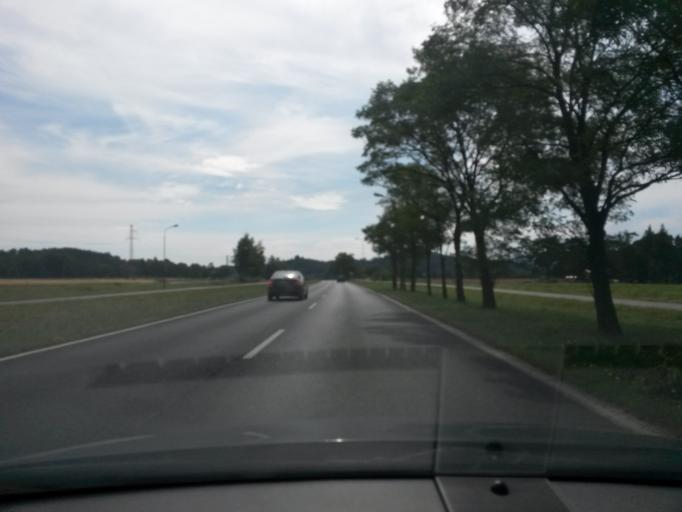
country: PL
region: Lower Silesian Voivodeship
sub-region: Powiat jeleniogorski
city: Jezow Sudecki
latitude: 50.9125
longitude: 15.7806
